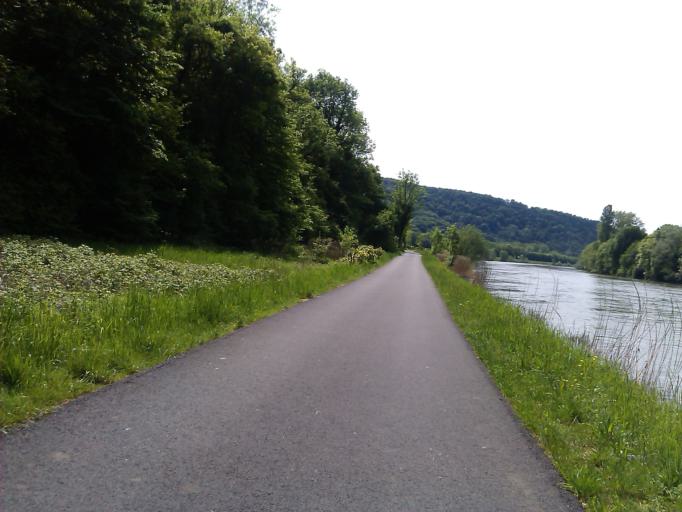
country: FR
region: Franche-Comte
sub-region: Departement du Doubs
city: Montferrand-le-Chateau
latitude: 47.1733
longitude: 5.9359
